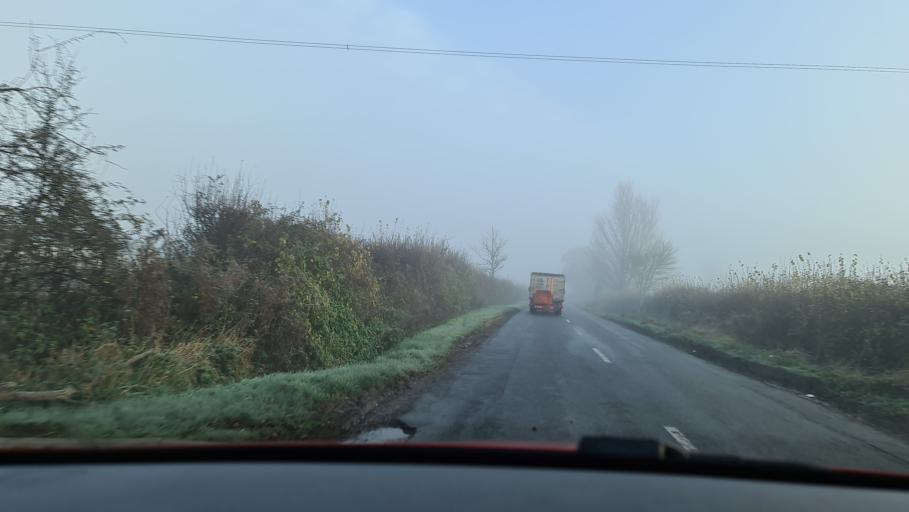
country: GB
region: England
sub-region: Buckinghamshire
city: Aylesbury
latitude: 51.7794
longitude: -0.8070
